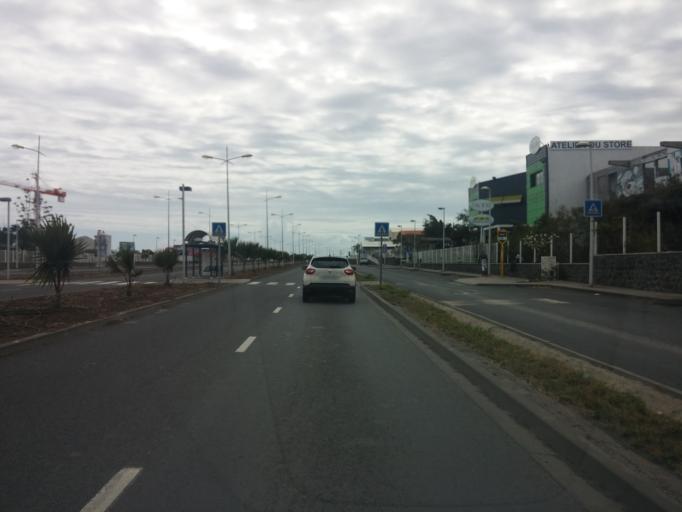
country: RE
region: Reunion
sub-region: Reunion
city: Le Port
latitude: -20.9641
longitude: 55.2945
